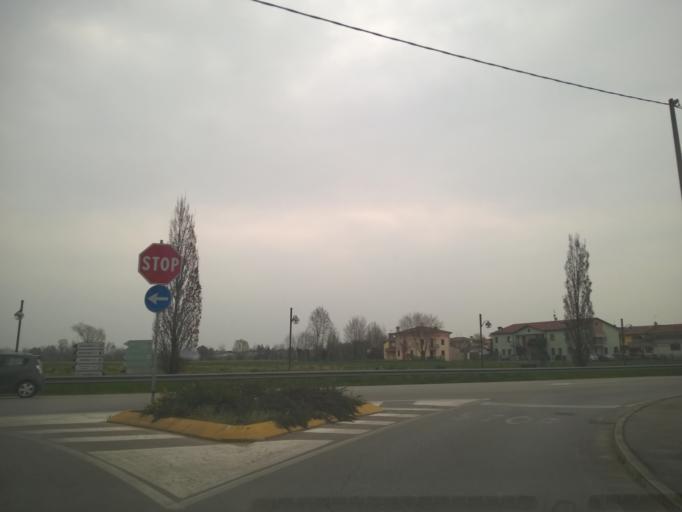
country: IT
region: Veneto
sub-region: Provincia di Vicenza
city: Poianella
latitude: 45.6359
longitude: 11.6261
